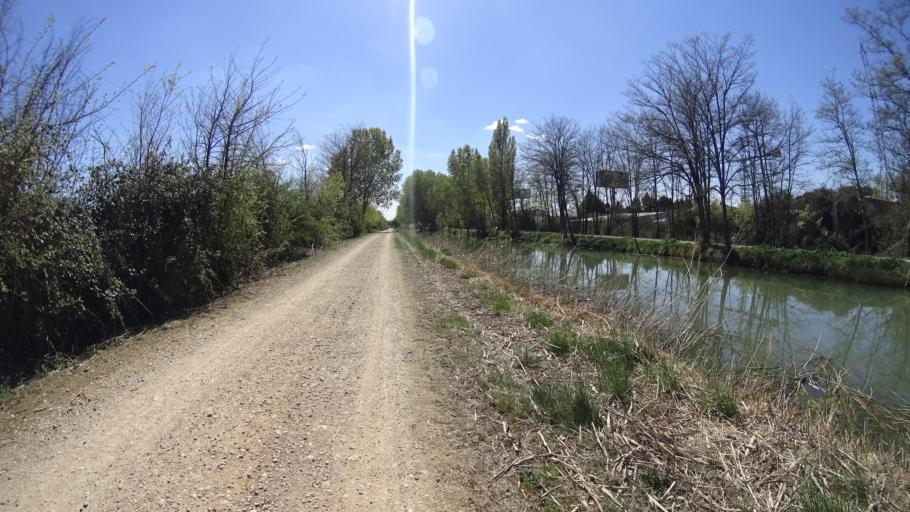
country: ES
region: Castille and Leon
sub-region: Provincia de Valladolid
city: Santovenia de Pisuerga
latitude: 41.7131
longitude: -4.6994
